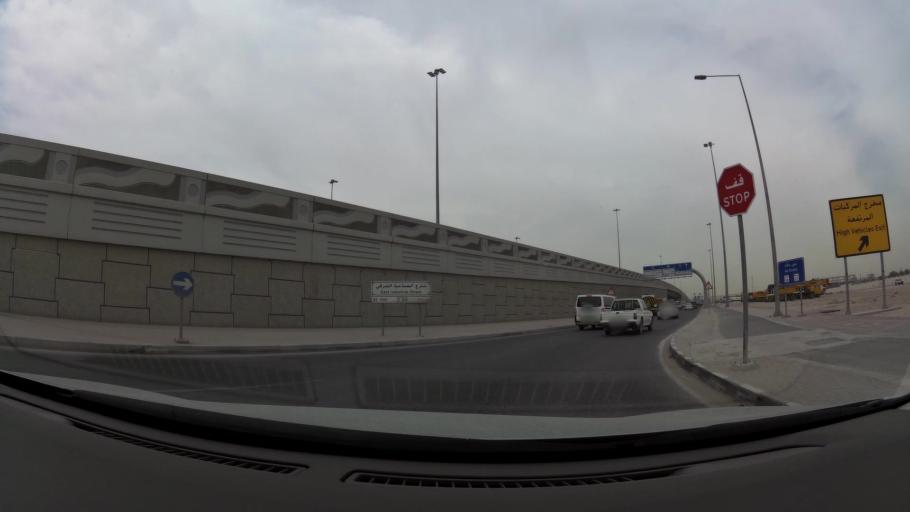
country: QA
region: Baladiyat ar Rayyan
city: Ar Rayyan
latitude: 25.2121
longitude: 51.4418
